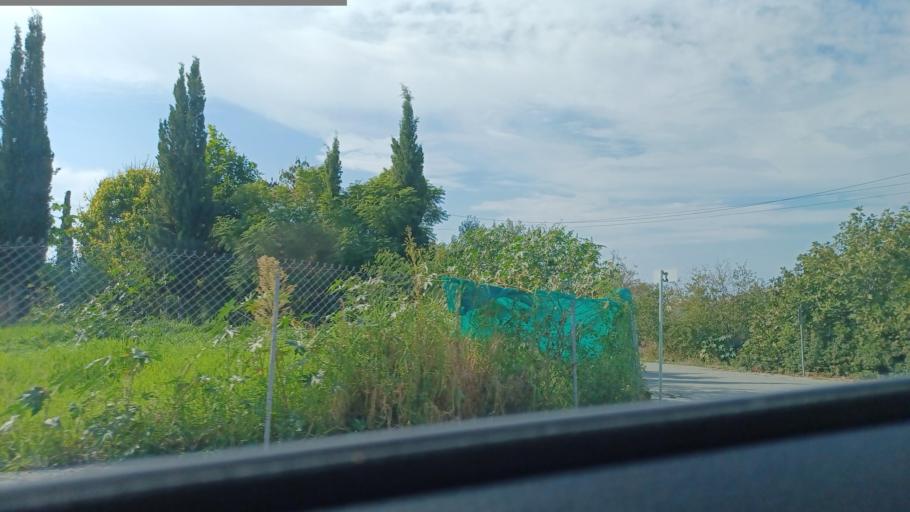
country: CY
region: Pafos
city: Pegeia
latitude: 34.8721
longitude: 32.3707
